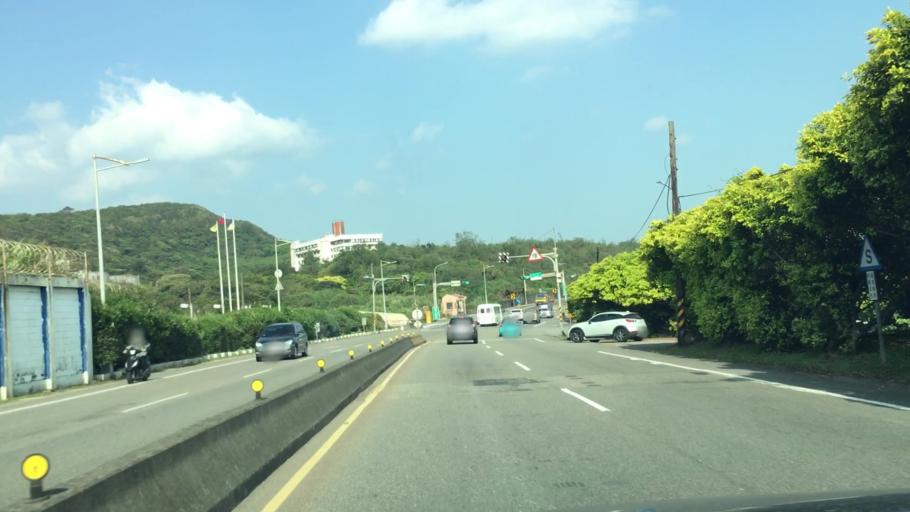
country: TW
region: Taiwan
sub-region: Keelung
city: Keelung
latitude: 25.2067
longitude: 121.6610
